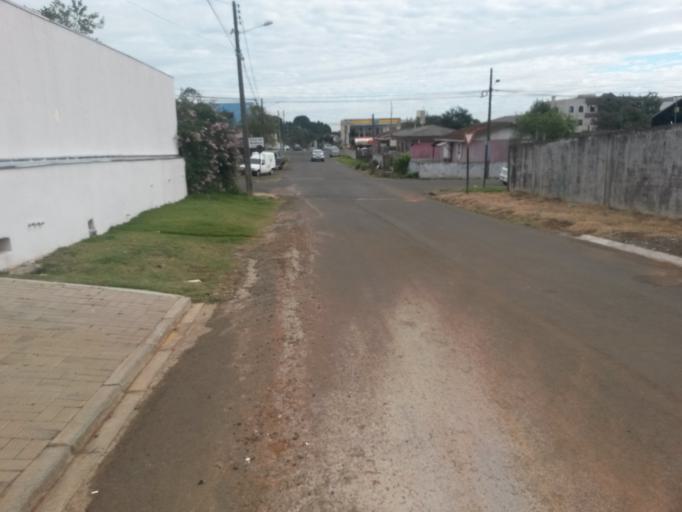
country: BR
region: Parana
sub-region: Guarapuava
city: Guarapuava
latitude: -25.3855
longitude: -51.4558
